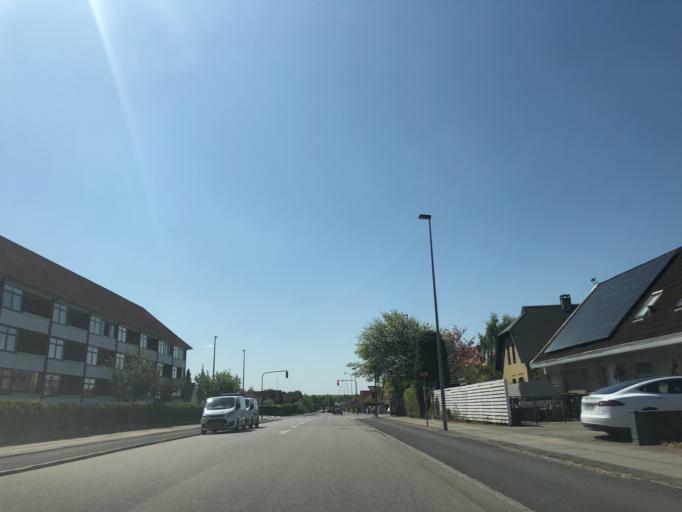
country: DK
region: Zealand
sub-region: Roskilde Kommune
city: Roskilde
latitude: 55.6376
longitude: 12.1027
